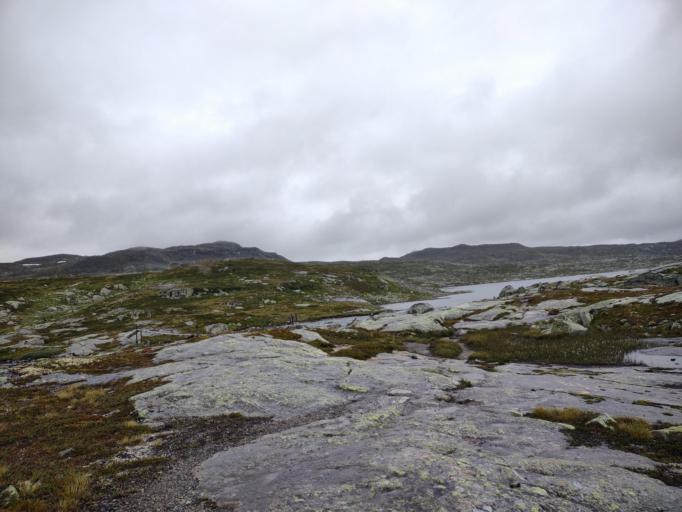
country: NO
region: Aust-Agder
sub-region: Bykle
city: Hovden
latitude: 59.9790
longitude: 7.2241
